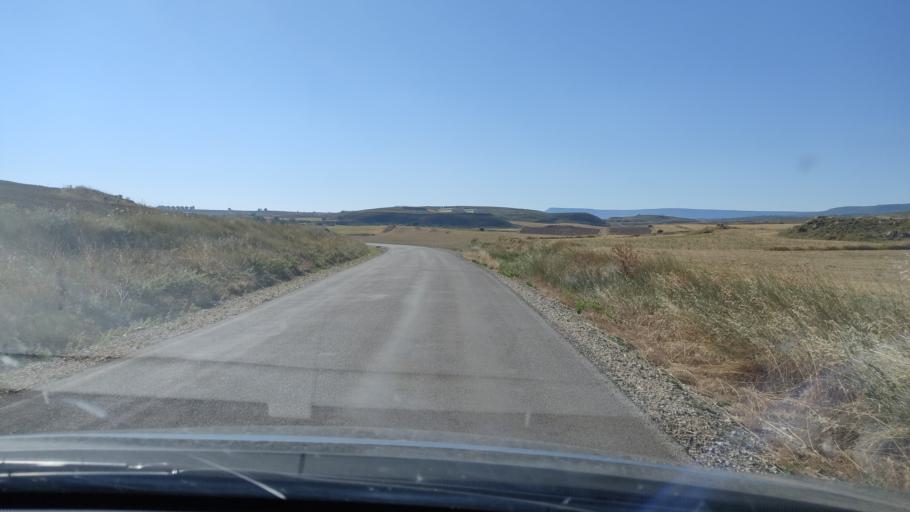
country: ES
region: Aragon
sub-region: Provincia de Teruel
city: Monforte de Moyuela
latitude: 41.0462
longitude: -1.0034
